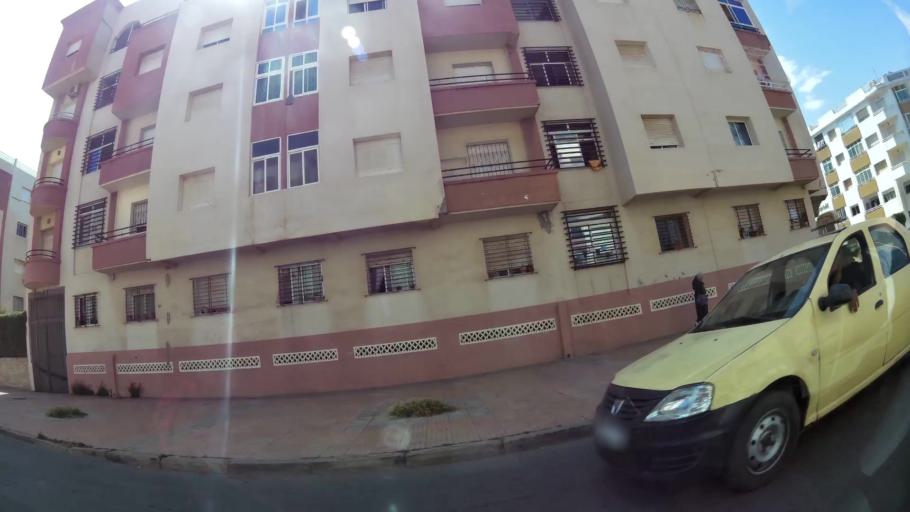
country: MA
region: Rabat-Sale-Zemmour-Zaer
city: Sale
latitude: 34.0752
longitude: -6.7927
